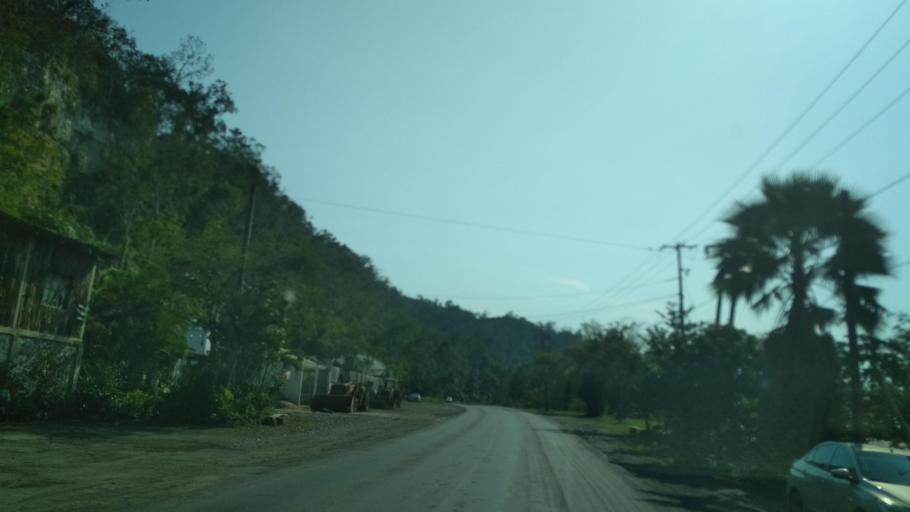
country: MX
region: Veracruz
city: Agua Dulce
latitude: 20.3993
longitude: -97.2308
